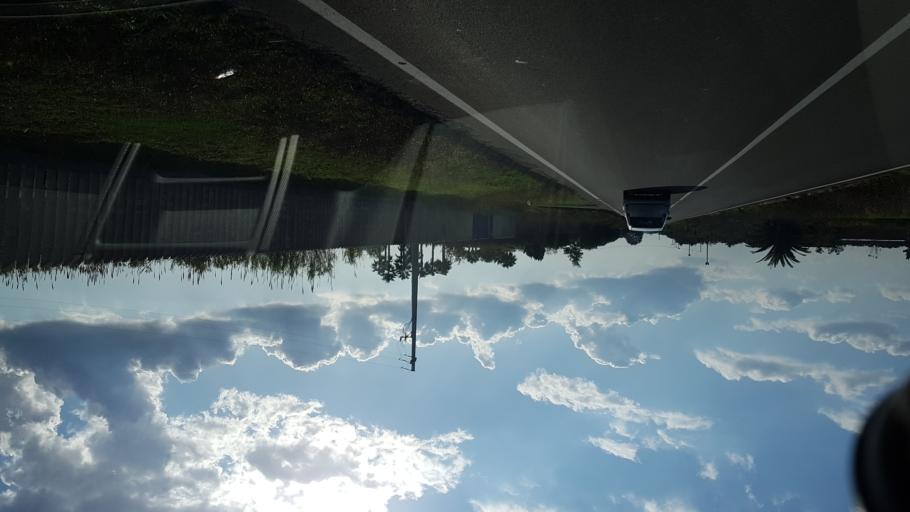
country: IT
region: Apulia
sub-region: Provincia di Lecce
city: Salice Salentino
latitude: 40.3655
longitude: 17.9674
